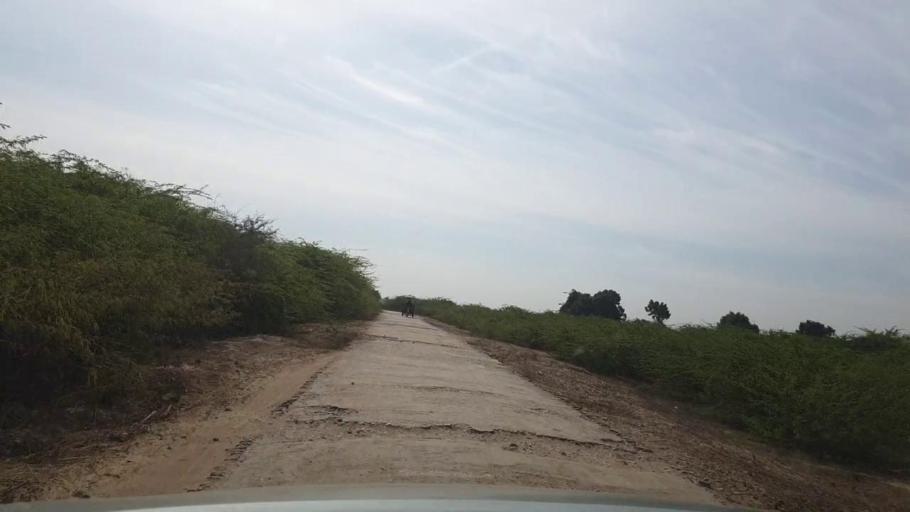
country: PK
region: Sindh
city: Kunri
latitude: 25.1609
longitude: 69.5966
